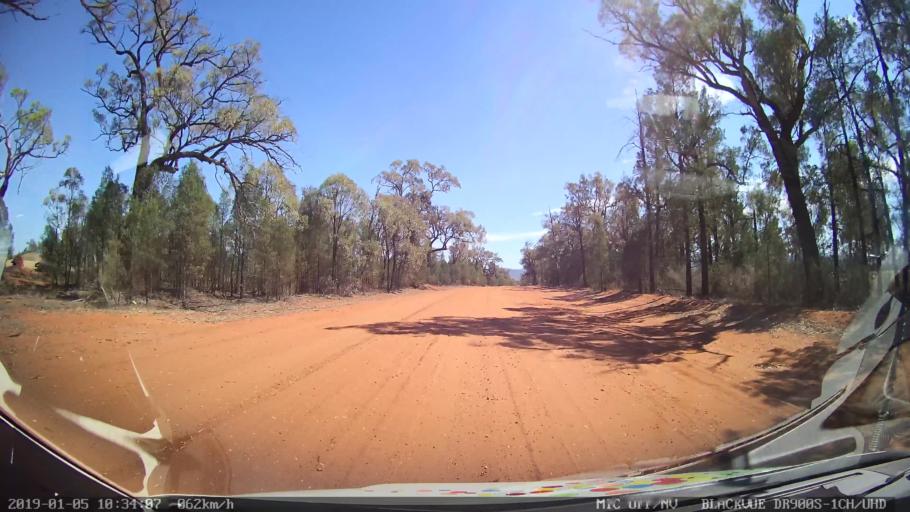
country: AU
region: New South Wales
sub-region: Gilgandra
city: Gilgandra
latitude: -31.5009
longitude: 148.9291
